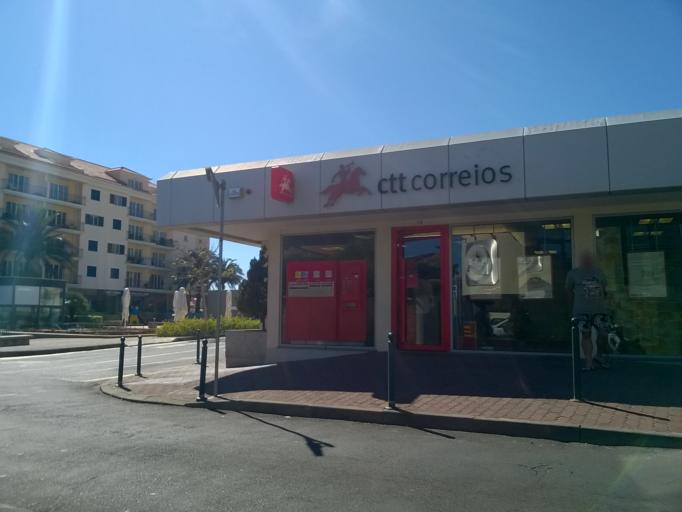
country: PT
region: Madeira
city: Canico
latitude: 32.6506
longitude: -16.8394
